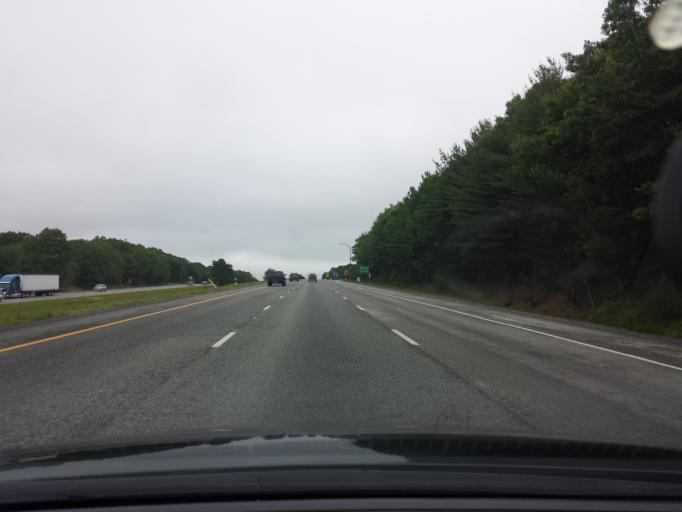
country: US
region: Rhode Island
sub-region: Washington County
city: Hope Valley
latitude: 41.5557
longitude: -71.6694
